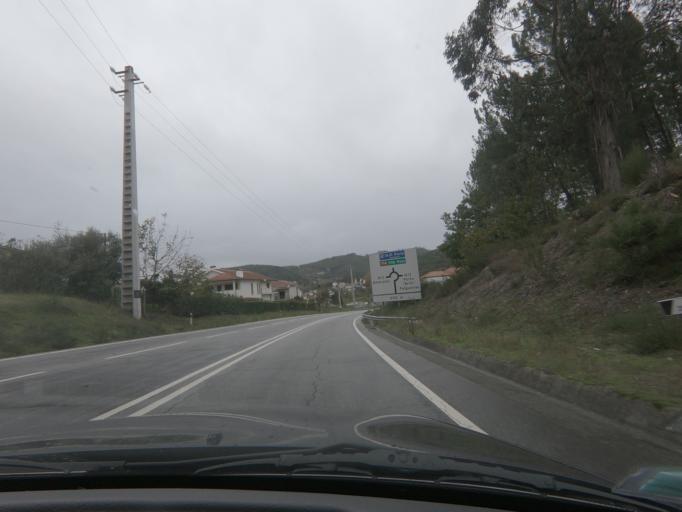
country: PT
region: Porto
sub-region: Amarante
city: Teloes
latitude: 41.2945
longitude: -8.0954
